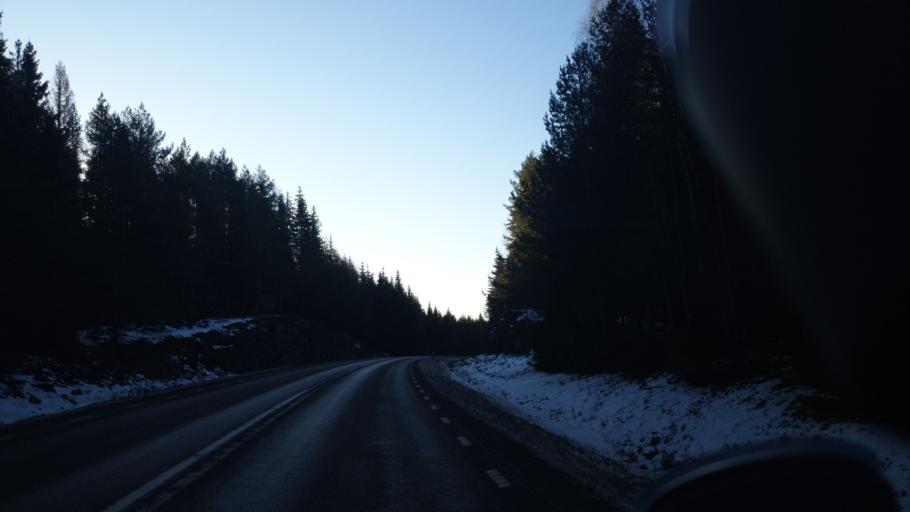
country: SE
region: Vaermland
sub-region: Arvika Kommun
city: Arvika
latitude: 59.7222
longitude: 12.5226
